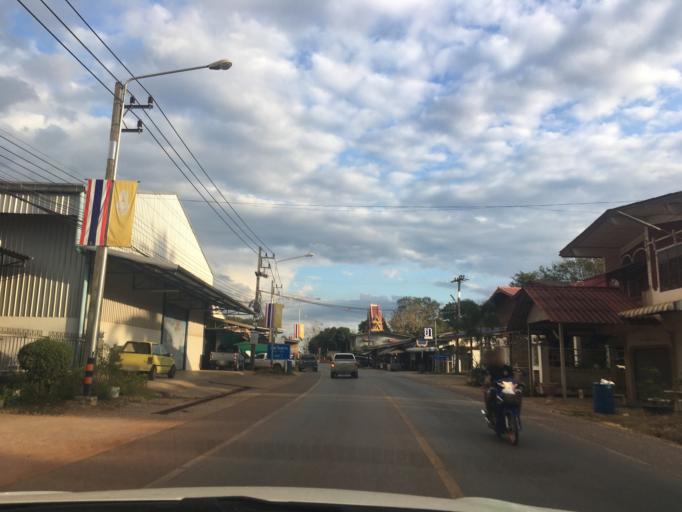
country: TH
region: Chanthaburi
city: Na Yai Am
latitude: 12.7281
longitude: 101.7517
